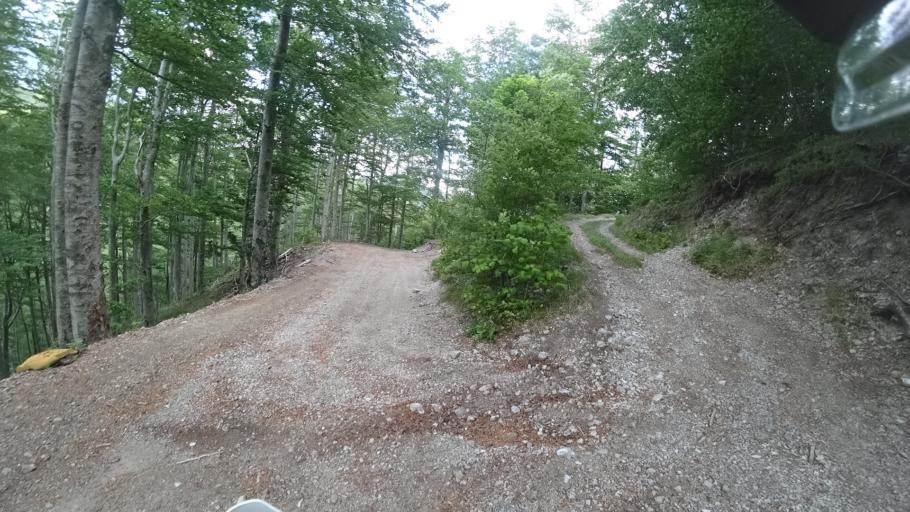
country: HR
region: Licko-Senjska
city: Gospic
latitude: 44.4398
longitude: 15.2993
